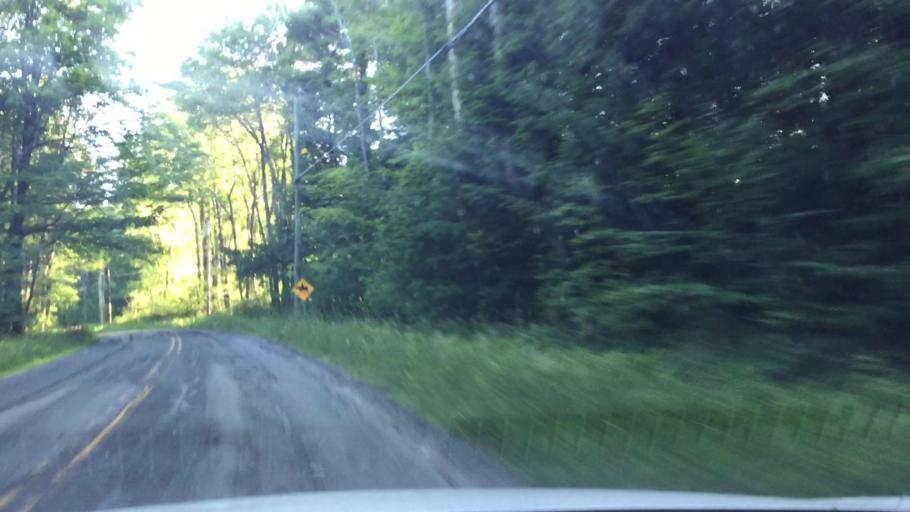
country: US
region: Massachusetts
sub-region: Berkshire County
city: Otis
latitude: 42.2455
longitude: -73.1116
